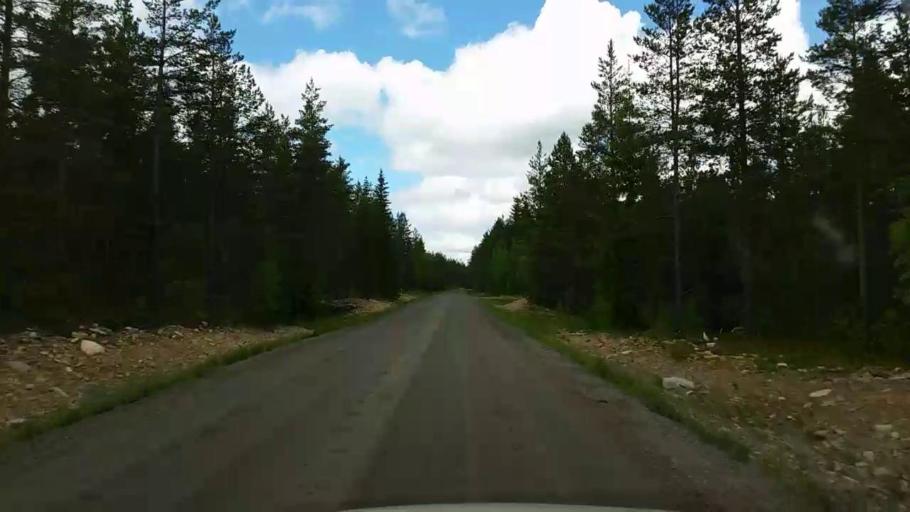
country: SE
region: Gaevleborg
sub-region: Bollnas Kommun
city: Vittsjo
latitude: 61.1562
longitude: 16.1597
